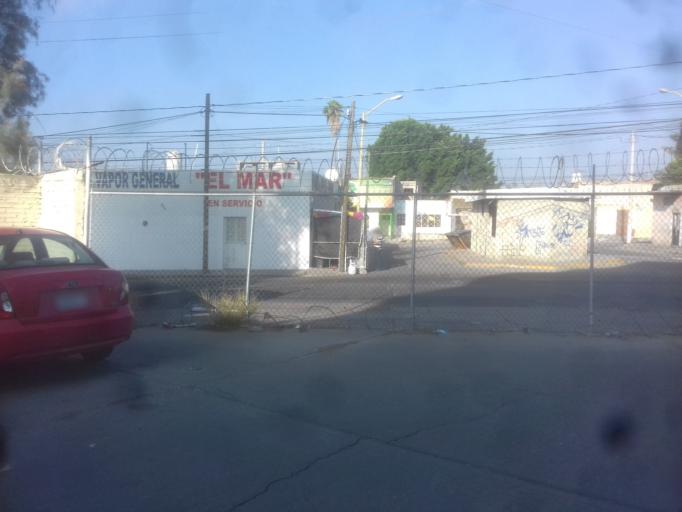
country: MX
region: Aguascalientes
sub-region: Aguascalientes
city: Aguascalientes
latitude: 21.8654
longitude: -102.2764
